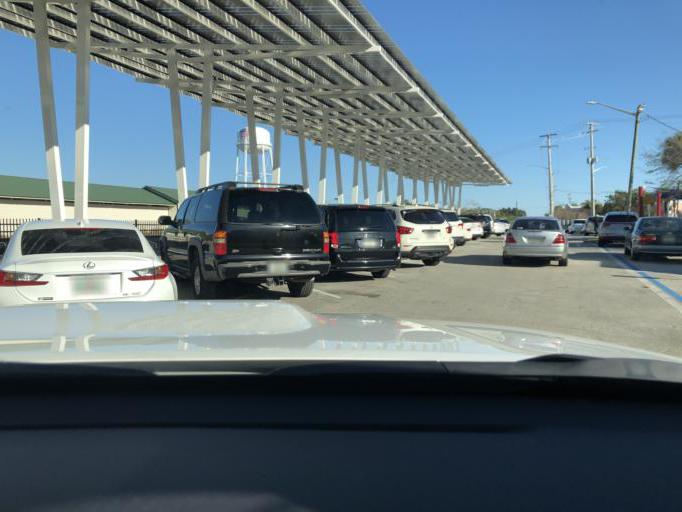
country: US
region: Florida
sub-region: Martin County
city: Stuart
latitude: 27.1965
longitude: -80.2521
